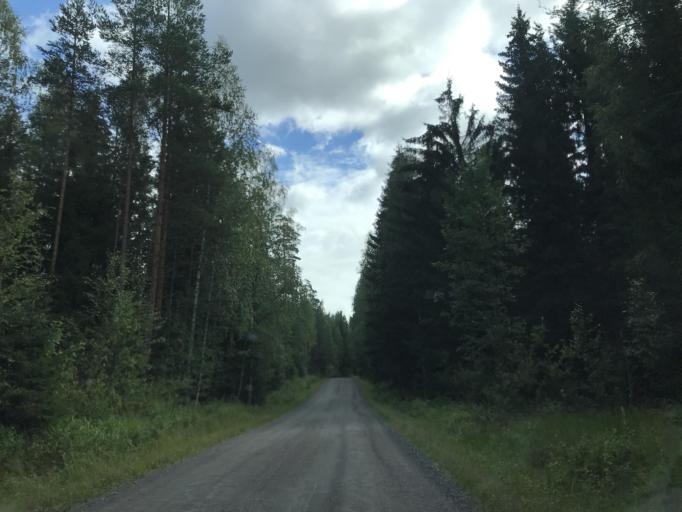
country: FI
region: Uusimaa
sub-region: Helsinki
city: Kaerkoelae
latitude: 60.6378
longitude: 23.7849
